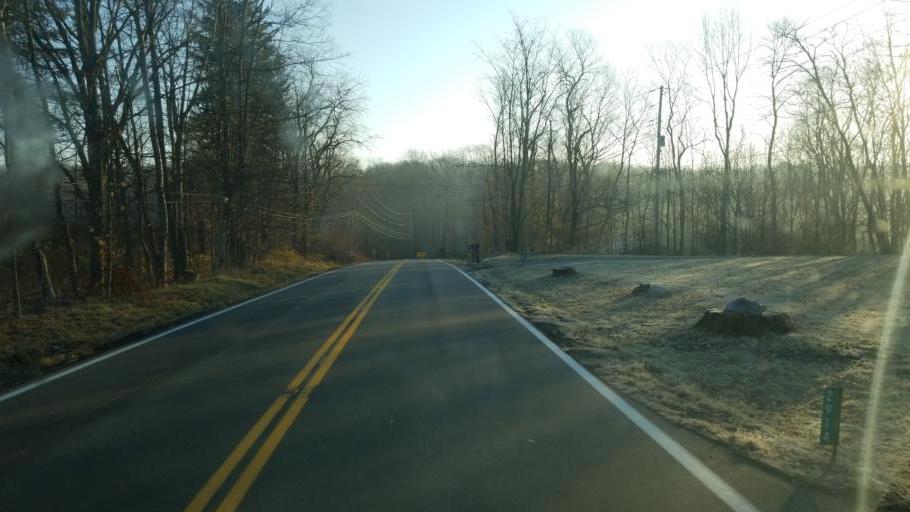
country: US
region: Ohio
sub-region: Medina County
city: Medina
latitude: 41.1065
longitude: -81.7925
